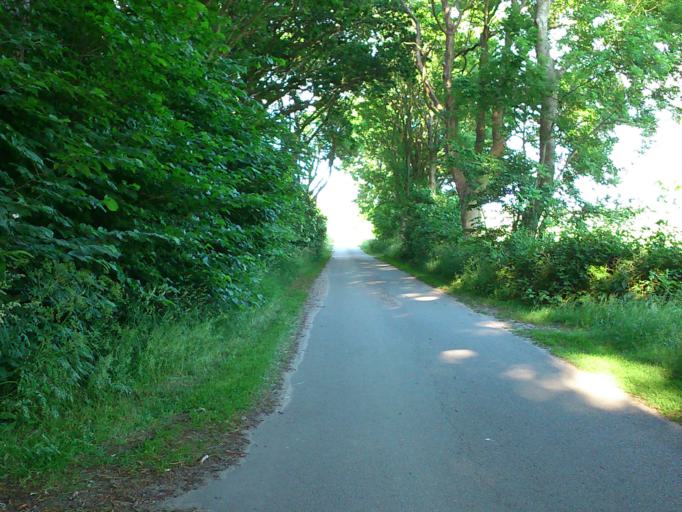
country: DK
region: Central Jutland
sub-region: Ringkobing-Skjern Kommune
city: Skjern
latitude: 55.9017
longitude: 8.4177
